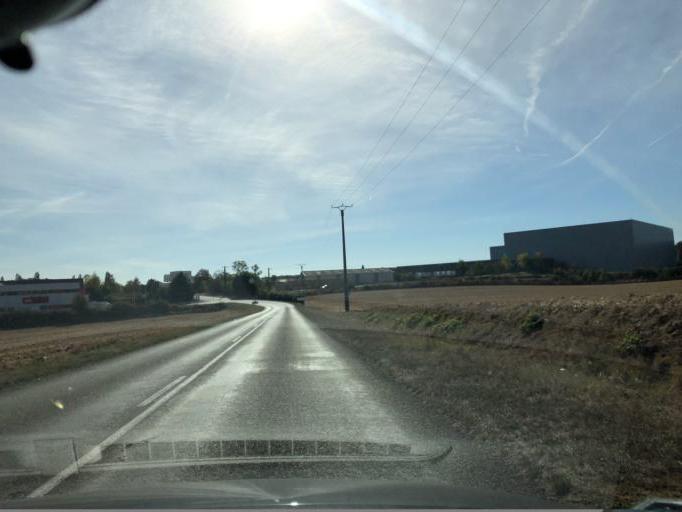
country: FR
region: Centre
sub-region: Departement du Loiret
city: Malesherbes
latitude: 48.3011
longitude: 2.3795
